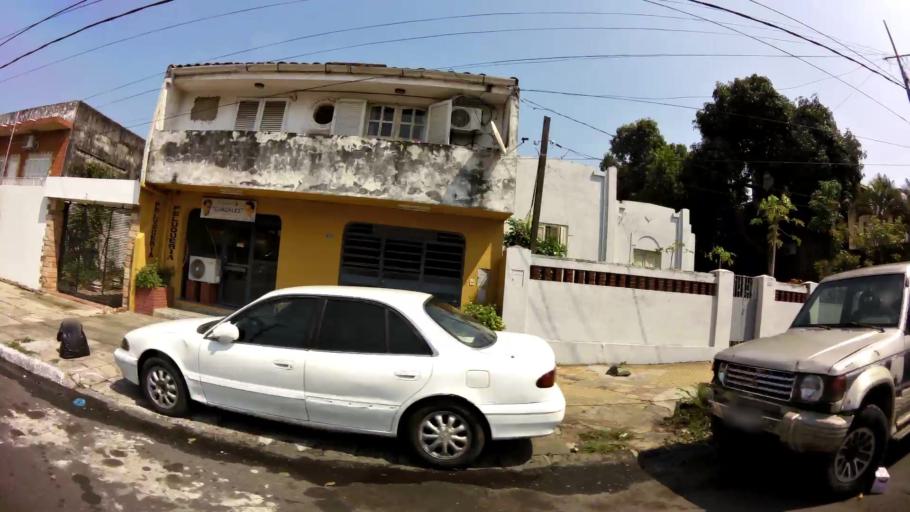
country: PY
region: Asuncion
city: Asuncion
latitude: -25.2925
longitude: -57.6514
